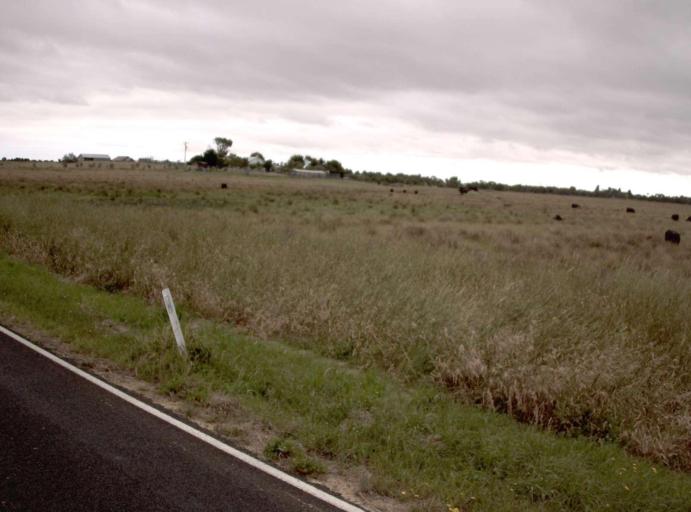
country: AU
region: Victoria
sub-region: Wellington
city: Sale
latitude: -38.5507
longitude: 146.8847
